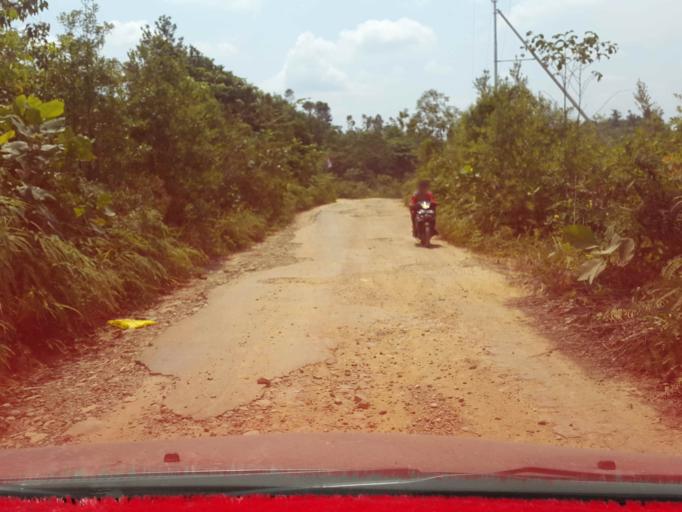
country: MY
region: Sarawak
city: Simanggang
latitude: 0.8485
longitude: 111.7705
